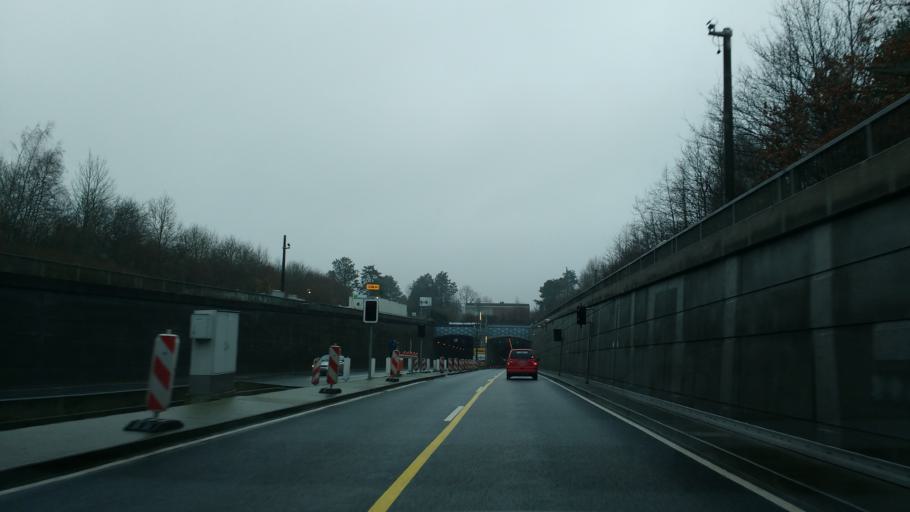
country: DE
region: Schleswig-Holstein
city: Westerronfeld
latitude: 54.2843
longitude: 9.6575
